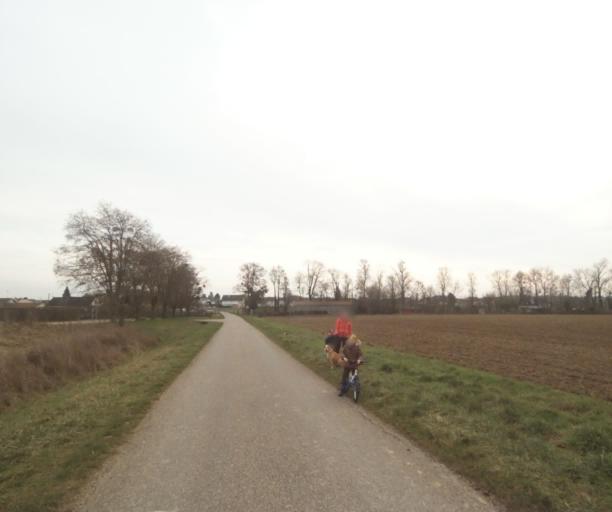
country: FR
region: Champagne-Ardenne
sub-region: Departement de la Haute-Marne
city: Villiers-en-Lieu
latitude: 48.6702
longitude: 4.8903
